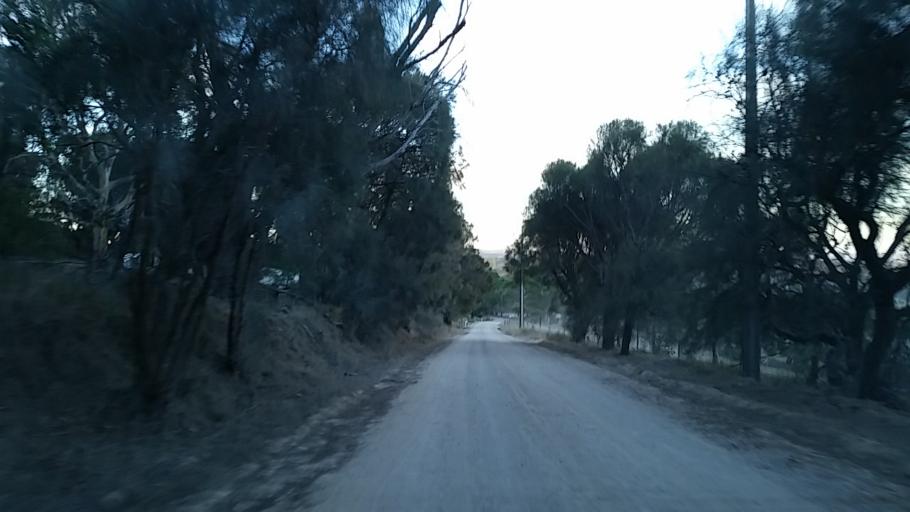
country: AU
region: South Australia
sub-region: Mount Barker
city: Nairne
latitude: -35.0623
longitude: 138.9242
